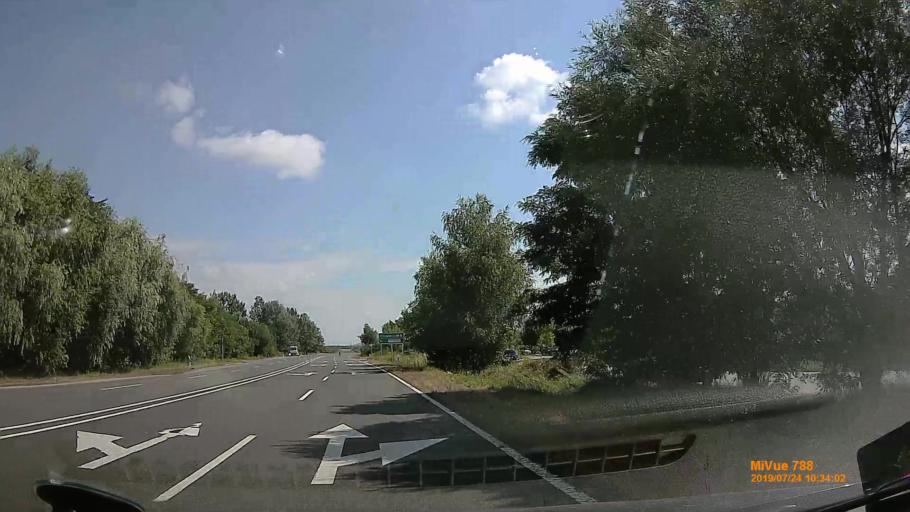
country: HU
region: Szabolcs-Szatmar-Bereg
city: Tarpa
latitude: 48.1601
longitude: 22.5600
